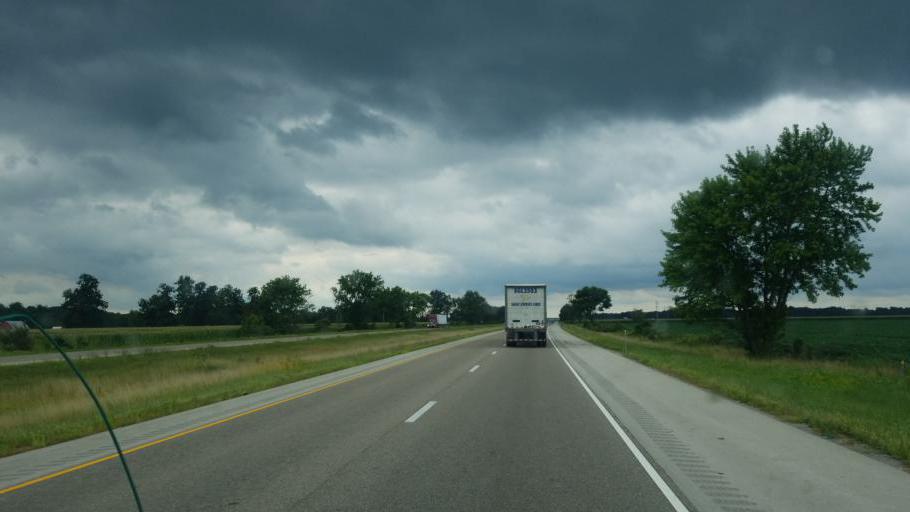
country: US
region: Illinois
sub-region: Cumberland County
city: Greenup
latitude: 39.2347
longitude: -88.2062
